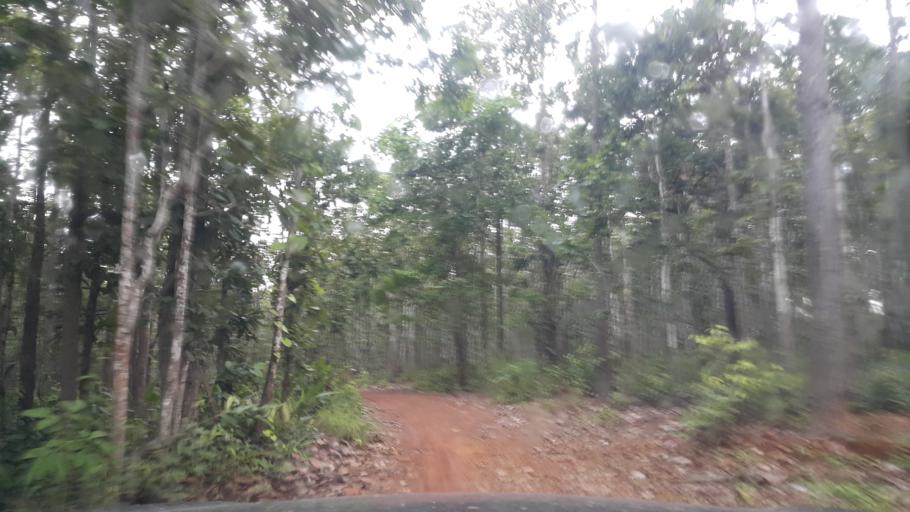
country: TH
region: Chiang Mai
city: San Sai
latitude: 18.9952
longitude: 99.1329
